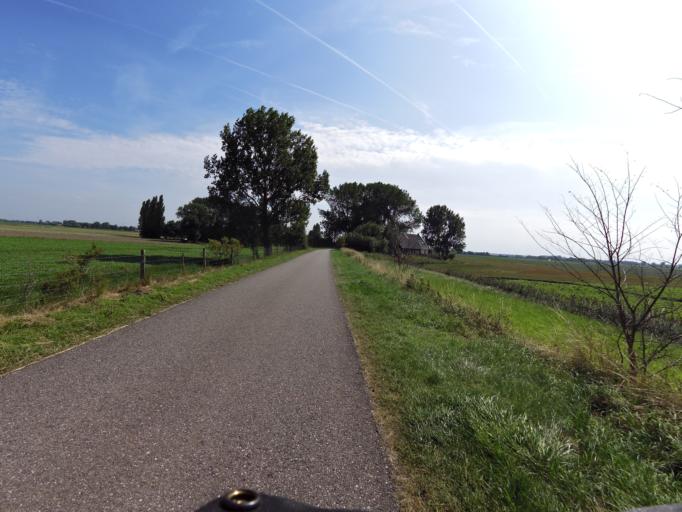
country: NL
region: North Brabant
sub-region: Gemeente Steenbergen
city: Dinteloord
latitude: 51.6929
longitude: 4.2971
